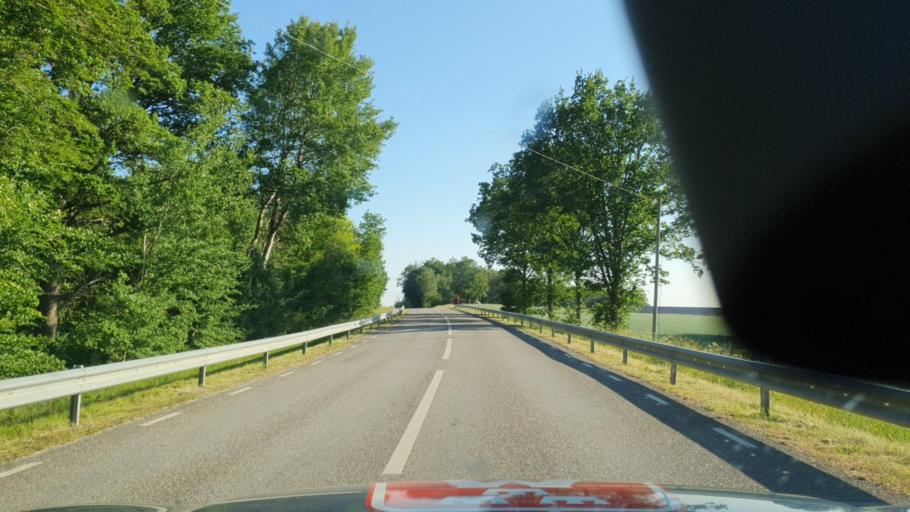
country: SE
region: Kalmar
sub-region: Kalmar Kommun
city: Ljungbyholm
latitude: 56.5141
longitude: 16.1535
